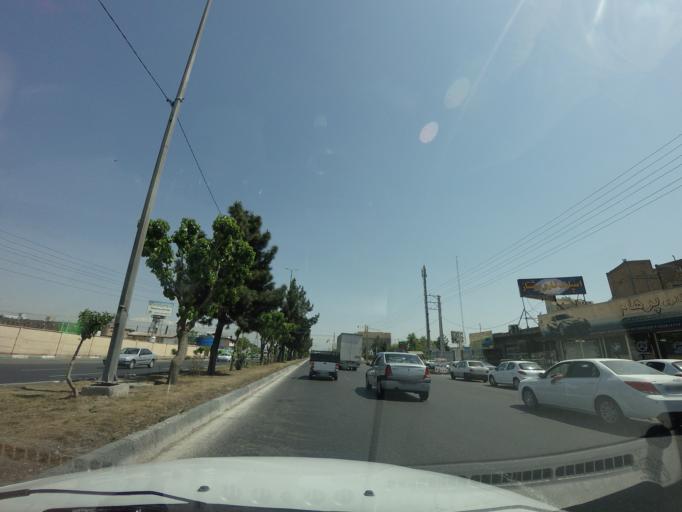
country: IR
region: Tehran
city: Eslamshahr
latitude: 35.6122
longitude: 51.3115
